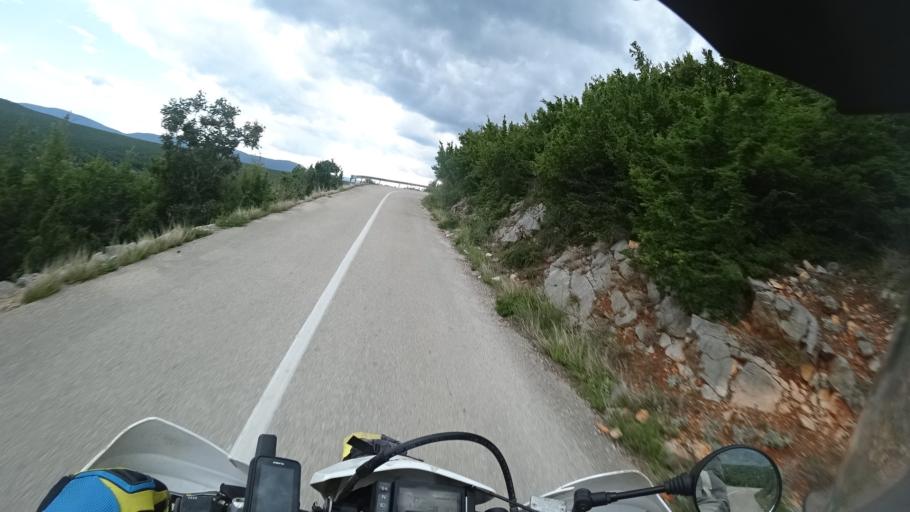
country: HR
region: Zadarska
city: Gracac
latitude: 44.1948
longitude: 15.8769
